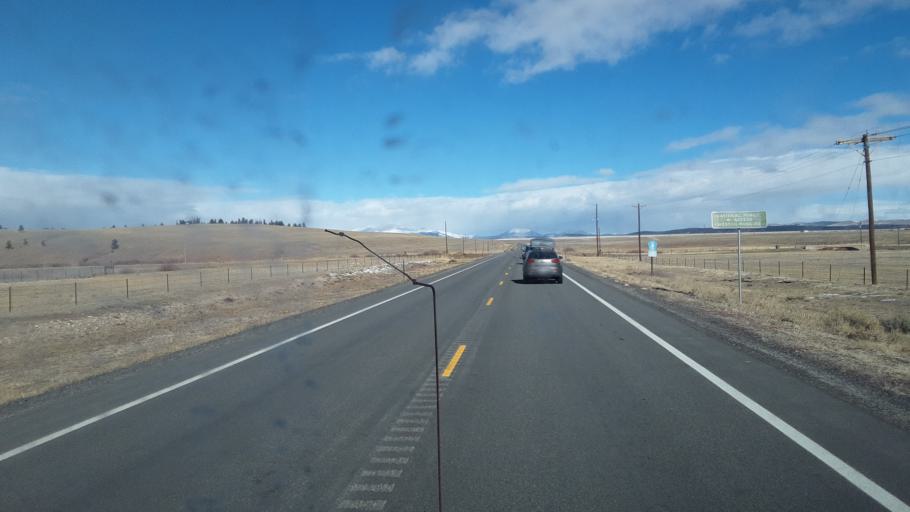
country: US
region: Colorado
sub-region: Park County
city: Fairplay
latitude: 39.0682
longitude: -105.9744
